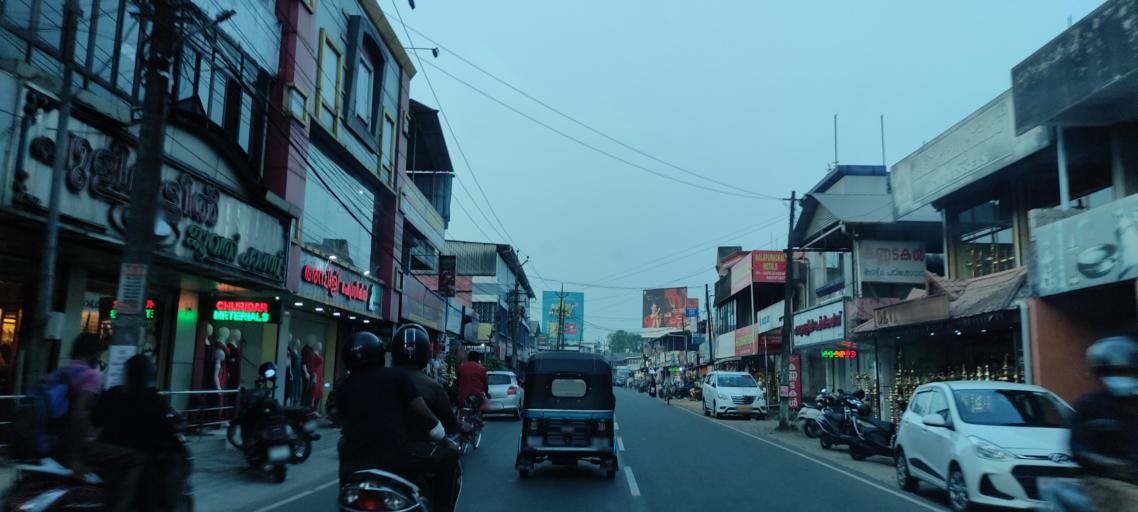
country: IN
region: Kerala
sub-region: Alappuzha
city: Mavelikara
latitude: 9.3208
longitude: 76.5335
